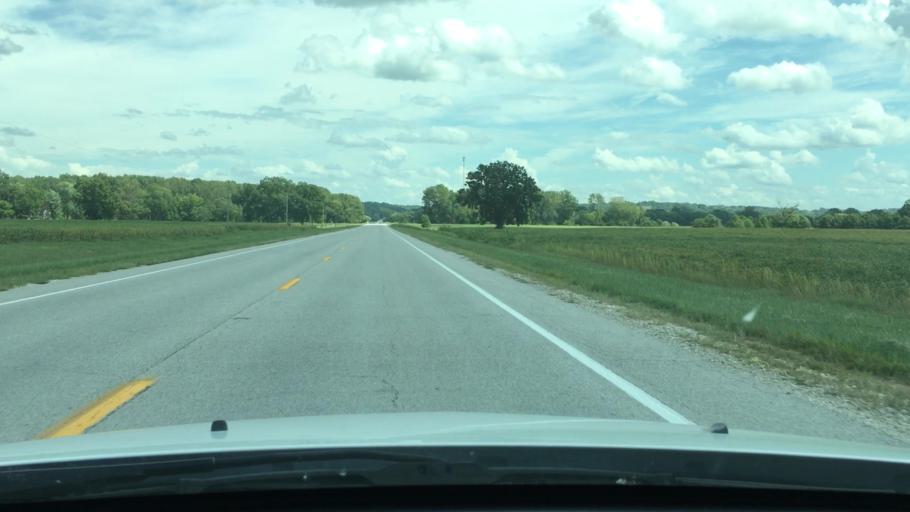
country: US
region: Missouri
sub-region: Pike County
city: Louisiana
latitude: 39.5010
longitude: -90.9954
